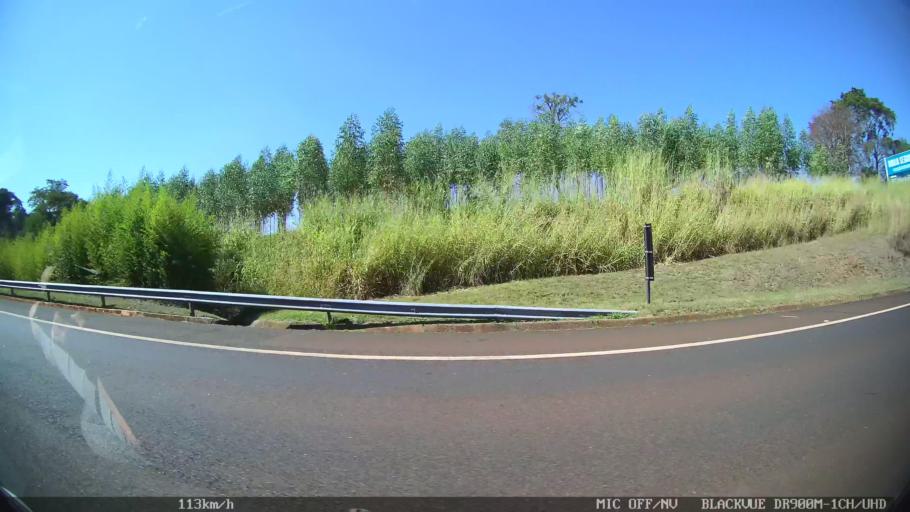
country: BR
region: Sao Paulo
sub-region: Franca
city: Franca
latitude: -20.6185
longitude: -47.4581
